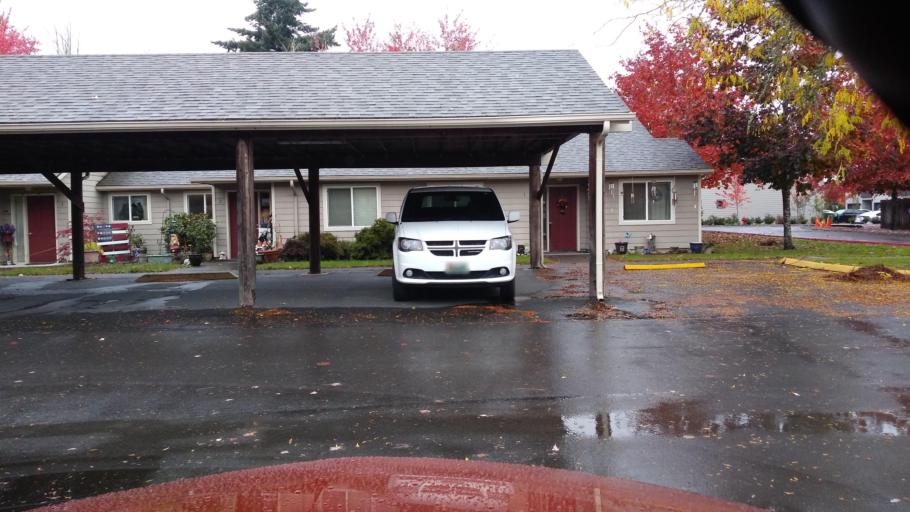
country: US
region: Oregon
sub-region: Washington County
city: Forest Grove
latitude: 45.5215
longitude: -123.0950
